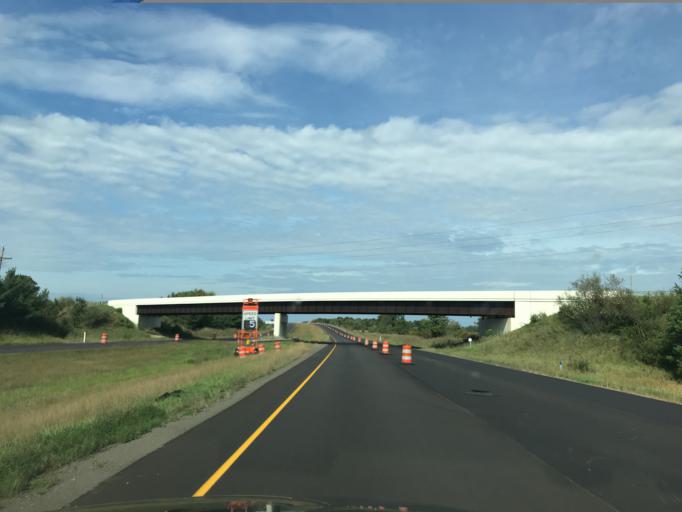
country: US
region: Ohio
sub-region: Ashtabula County
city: Jefferson
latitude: 41.7957
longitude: -80.7428
